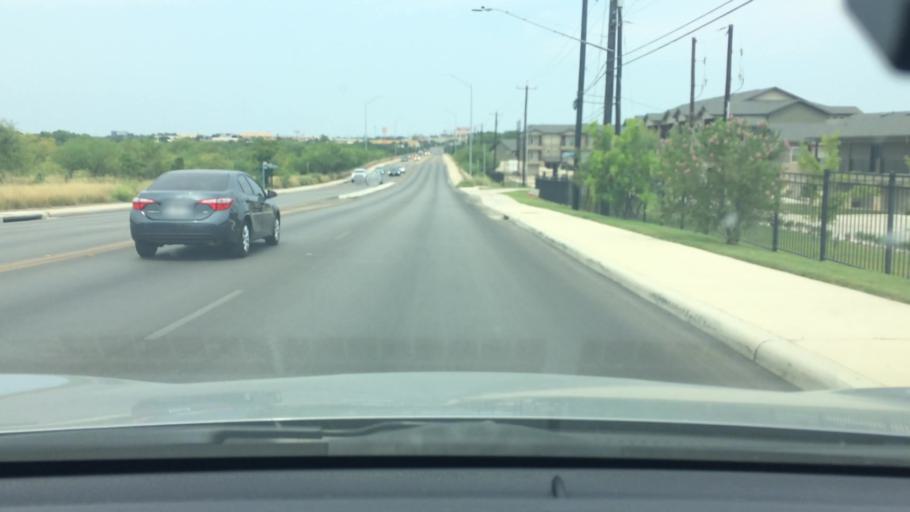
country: US
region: Texas
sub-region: Bexar County
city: Leon Valley
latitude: 29.4615
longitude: -98.6327
